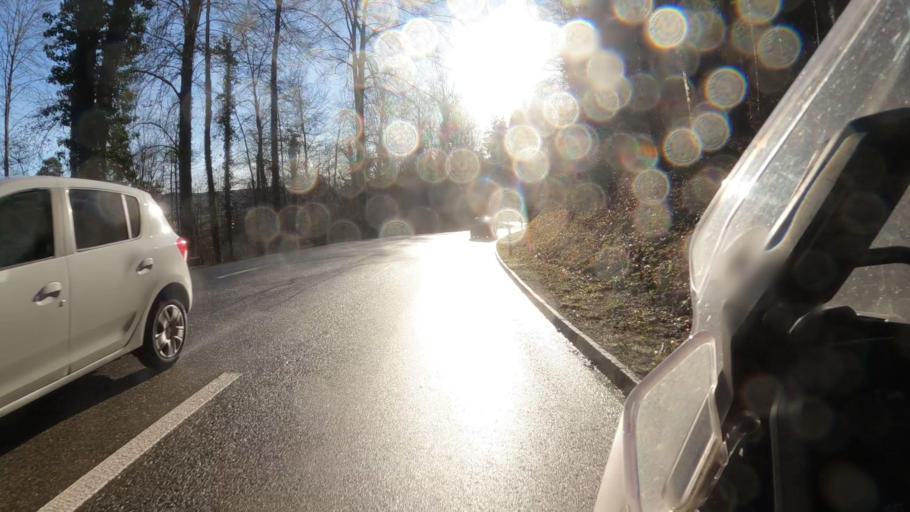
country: CH
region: Zurich
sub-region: Bezirk Buelach
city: Rorbas
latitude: 47.5185
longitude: 8.5777
